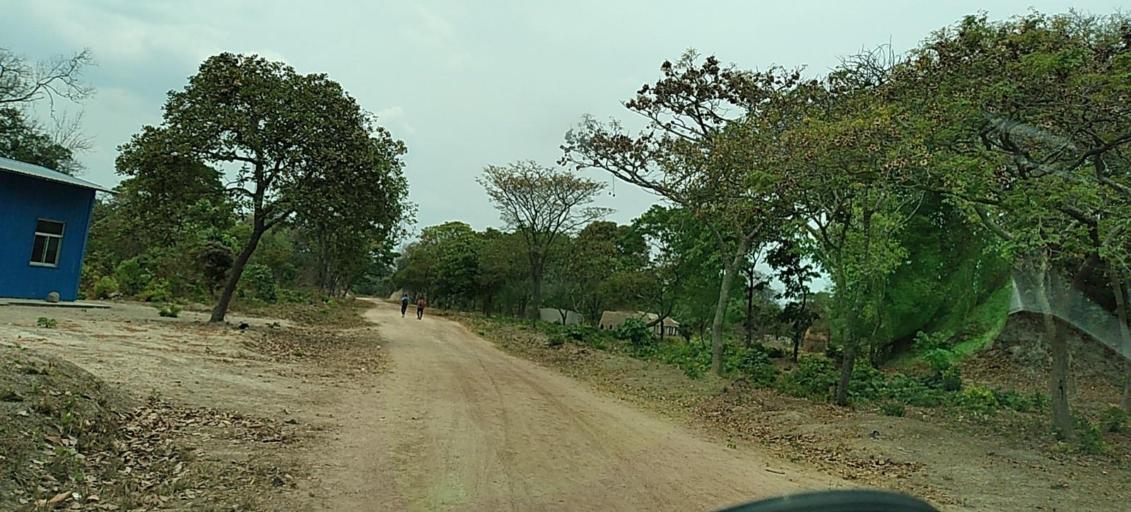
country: ZM
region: North-Western
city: Solwezi
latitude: -12.7845
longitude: 26.5162
